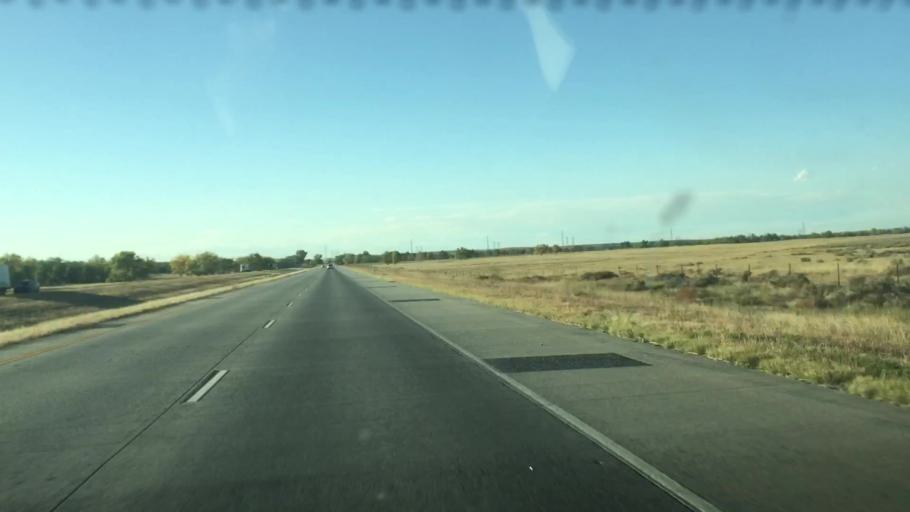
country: US
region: Colorado
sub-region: Arapahoe County
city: Byers
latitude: 39.6469
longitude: -104.0681
